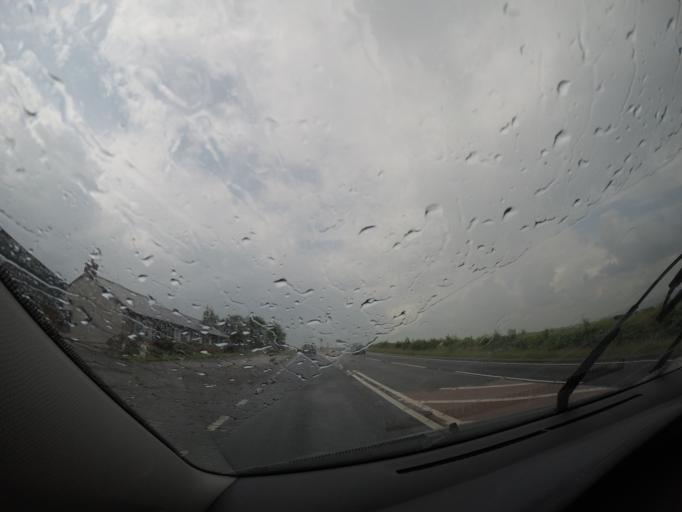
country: GB
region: England
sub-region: Cumbria
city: Appleby-in-Westmorland
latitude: 54.6278
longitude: -2.5808
